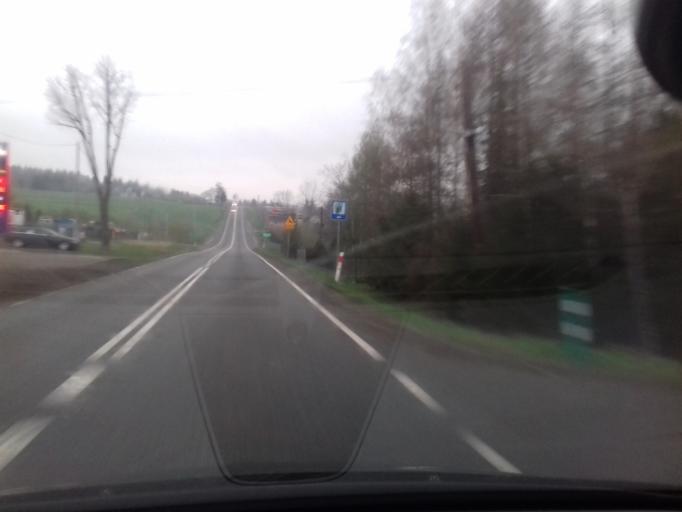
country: PL
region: Lesser Poland Voivodeship
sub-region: Powiat limanowski
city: Tymbark
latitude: 49.7224
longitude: 20.3190
